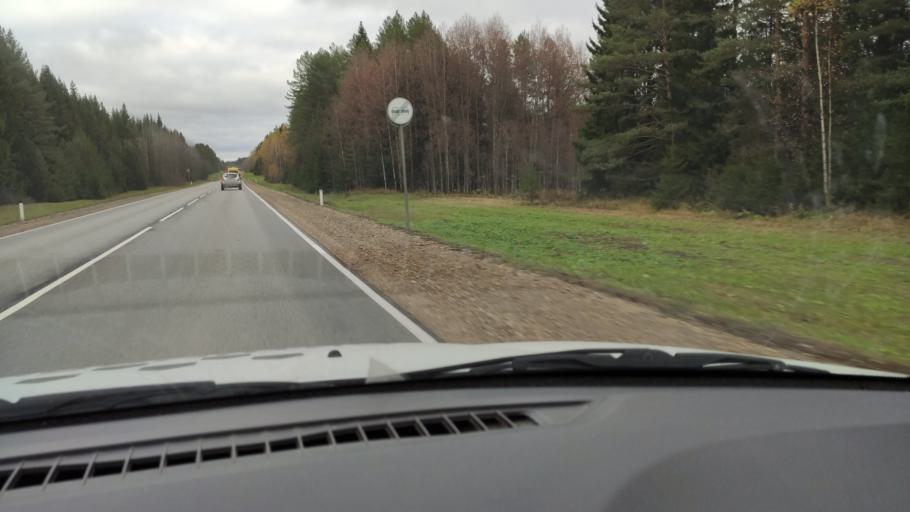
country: RU
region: Kirov
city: Slobodskoy
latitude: 58.7685
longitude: 50.3661
